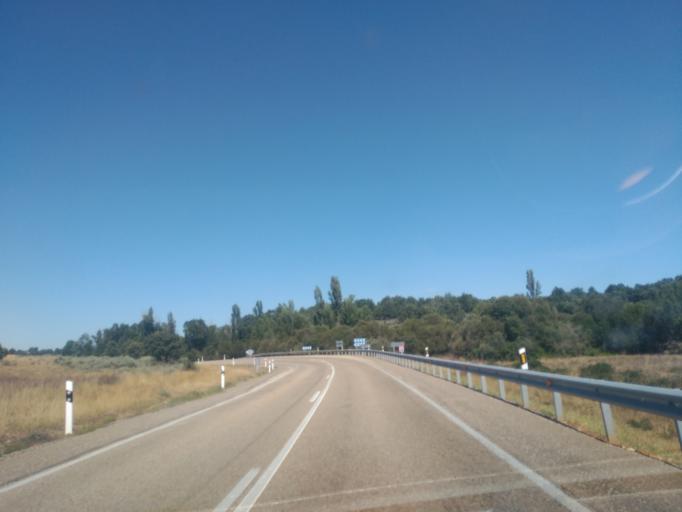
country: ES
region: Castille and Leon
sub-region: Provincia de Zamora
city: Ferreras de Arriba
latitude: 41.9532
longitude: -6.2043
